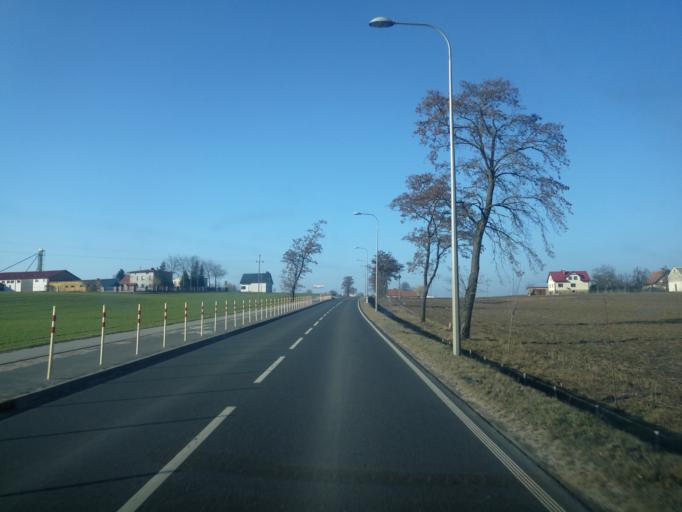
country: PL
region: Warmian-Masurian Voivodeship
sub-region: Powiat ilawski
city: Lubawa
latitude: 53.4619
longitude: 19.7746
